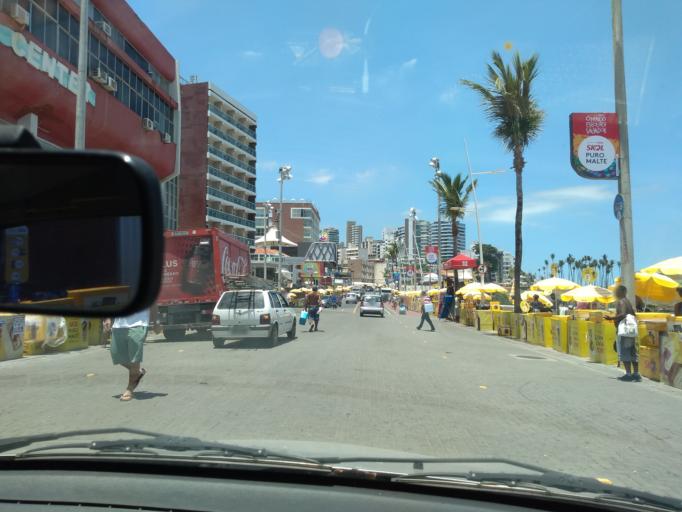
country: BR
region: Bahia
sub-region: Salvador
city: Salvador
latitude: -13.0095
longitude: -38.5273
